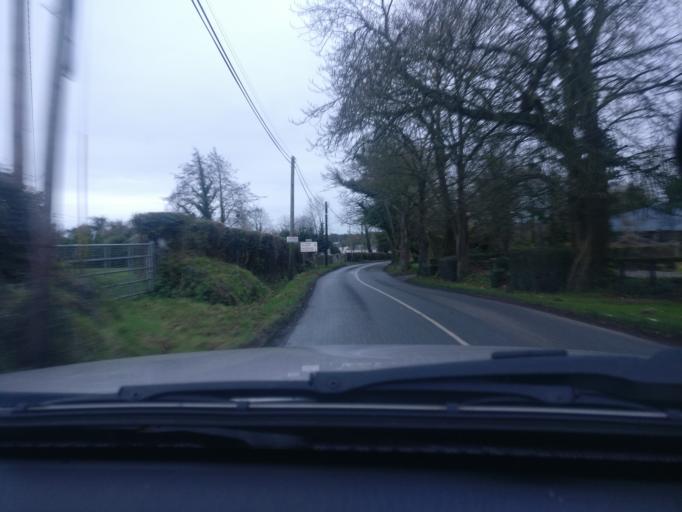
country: IE
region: Leinster
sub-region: An Mhi
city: Dunshaughlin
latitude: 53.5013
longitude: -6.5997
